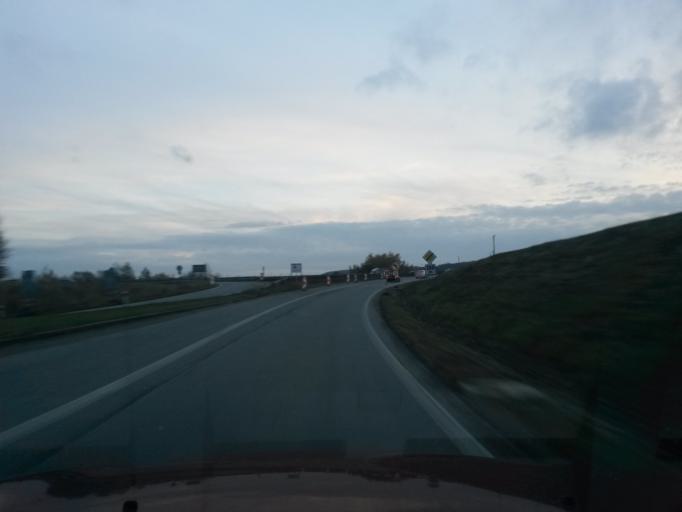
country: SK
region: Kosicky
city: Kosice
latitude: 48.7890
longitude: 21.3074
